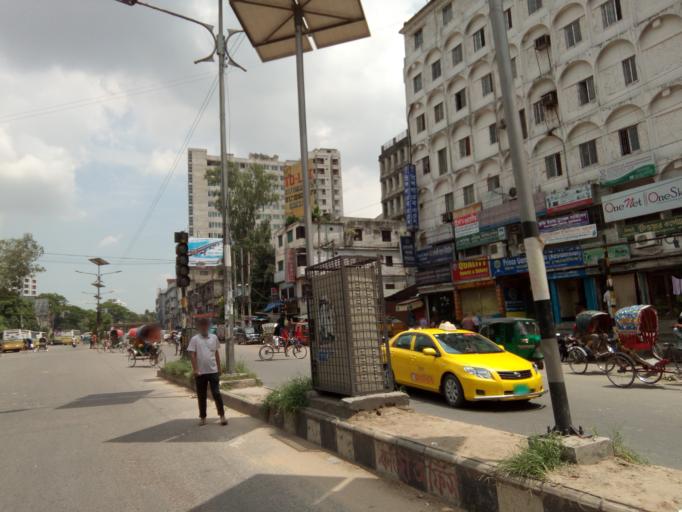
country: BD
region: Dhaka
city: Paltan
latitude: 23.7330
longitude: 90.4195
